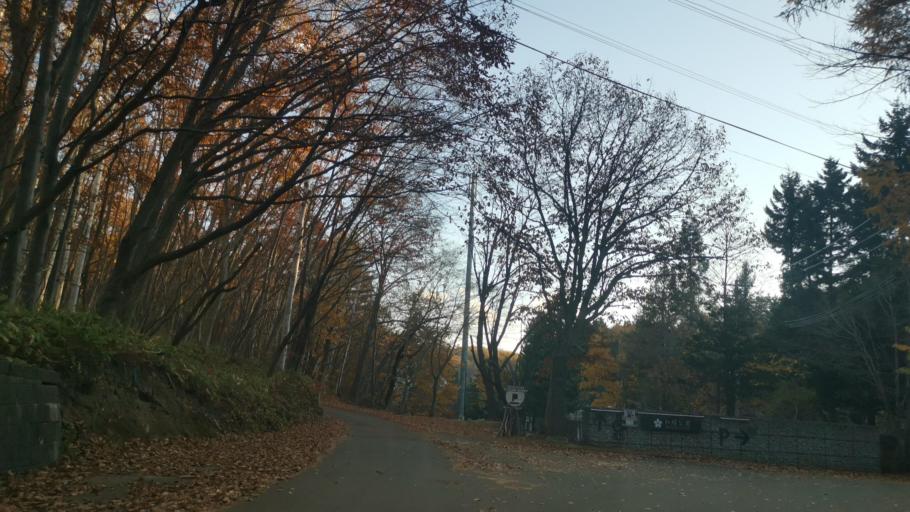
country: JP
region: Hokkaido
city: Sapporo
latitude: 42.9929
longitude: 141.3659
